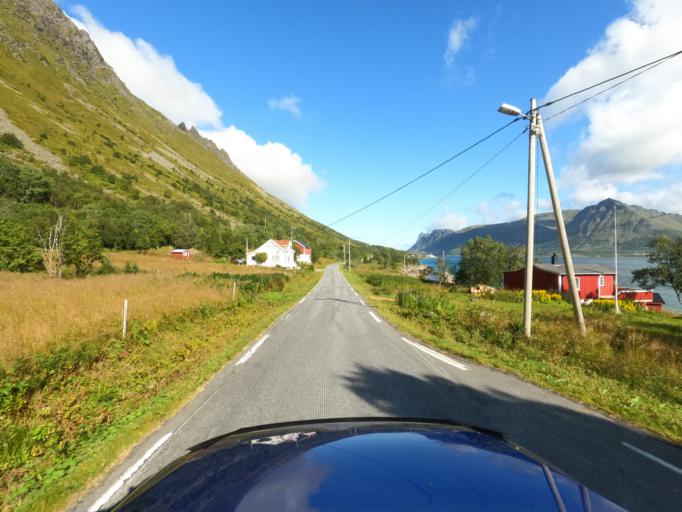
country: NO
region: Nordland
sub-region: Vagan
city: Kabelvag
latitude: 68.2721
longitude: 14.2511
